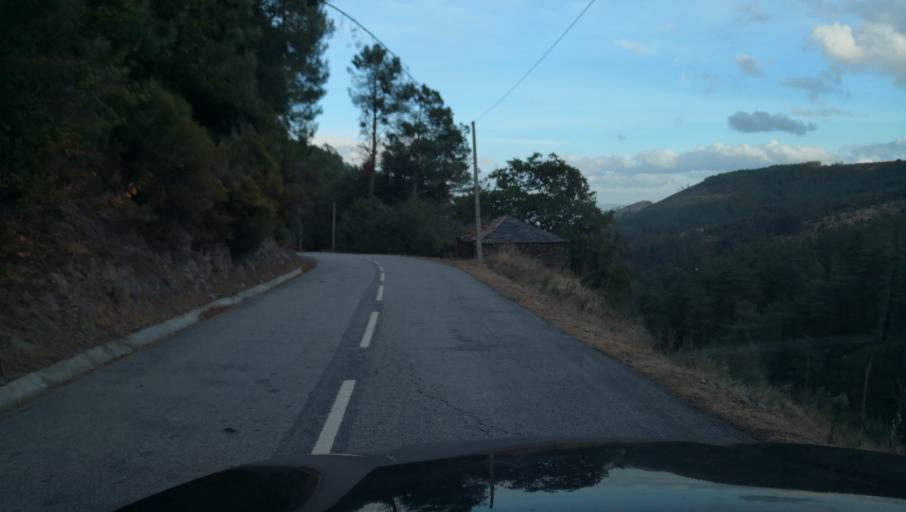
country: PT
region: Vila Real
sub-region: Santa Marta de Penaguiao
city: Santa Marta de Penaguiao
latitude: 41.2439
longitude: -7.8543
